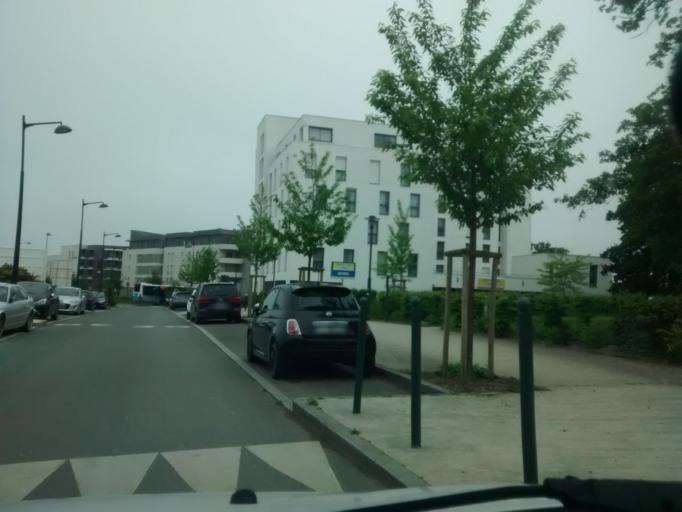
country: FR
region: Brittany
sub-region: Departement d'Ille-et-Vilaine
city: Saint-Gregoire
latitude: 48.1319
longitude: -1.6964
